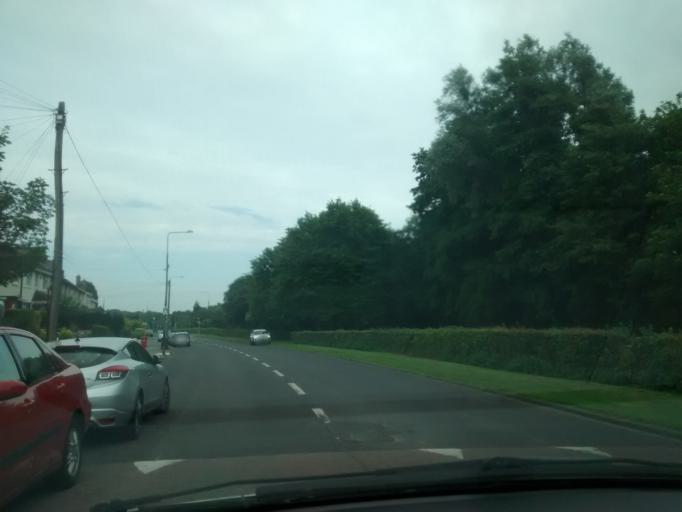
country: IE
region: Leinster
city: Dollymount
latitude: 53.3756
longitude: -6.1879
